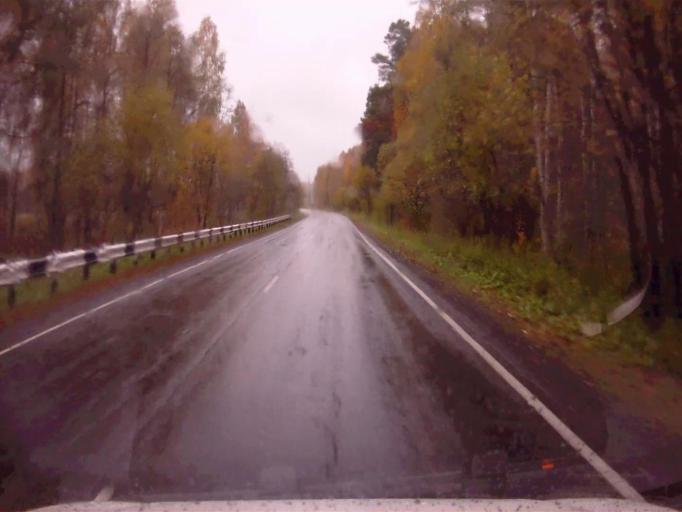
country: RU
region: Chelyabinsk
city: Verkhniy Ufaley
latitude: 55.9421
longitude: 60.4089
